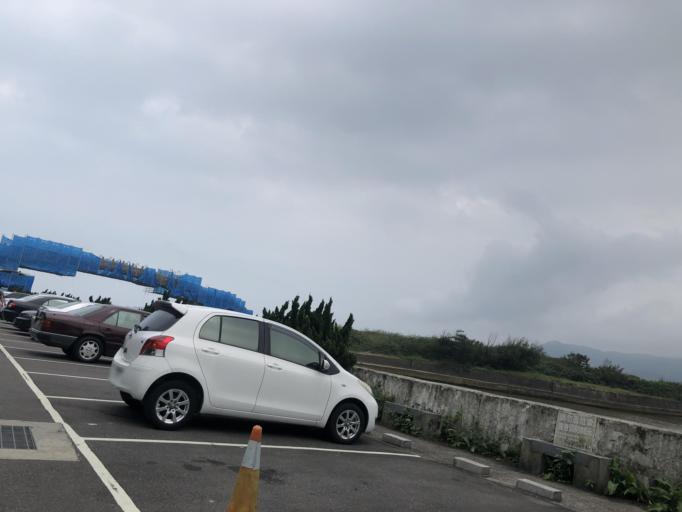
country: TW
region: Taiwan
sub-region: Keelung
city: Keelung
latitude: 25.2238
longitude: 121.6479
